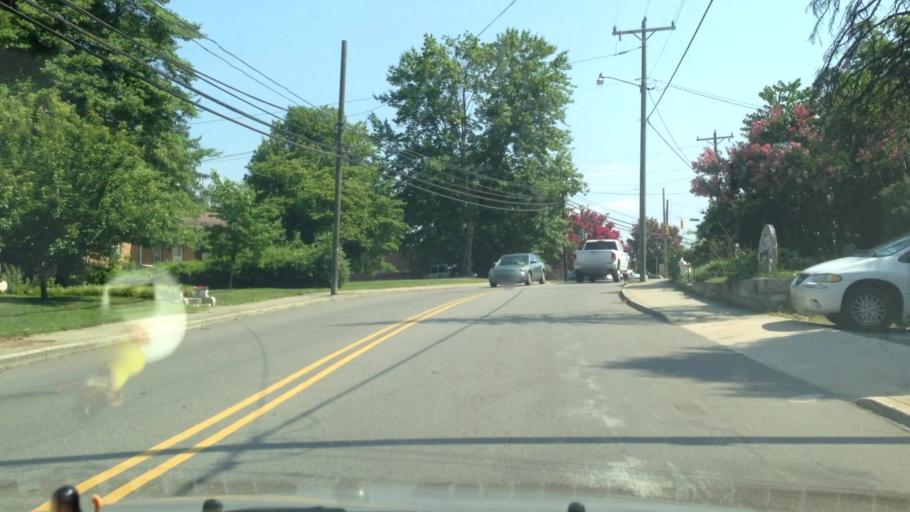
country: US
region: North Carolina
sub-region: Surry County
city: Mount Airy
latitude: 36.4966
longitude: -80.6094
